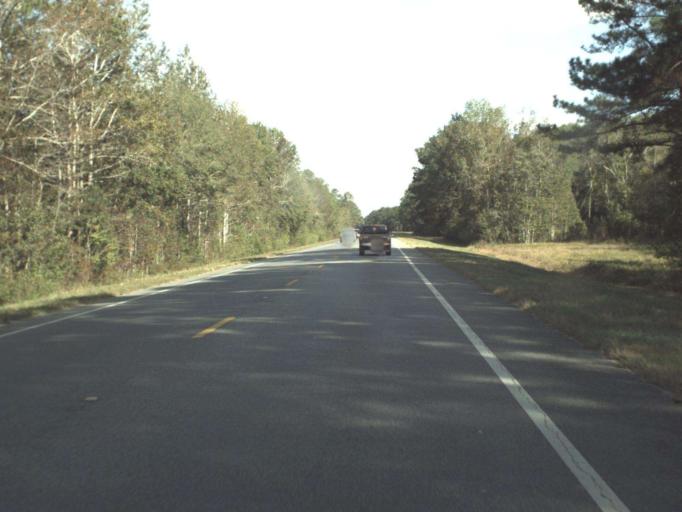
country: US
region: Florida
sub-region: Holmes County
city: Bonifay
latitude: 30.7782
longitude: -85.6105
